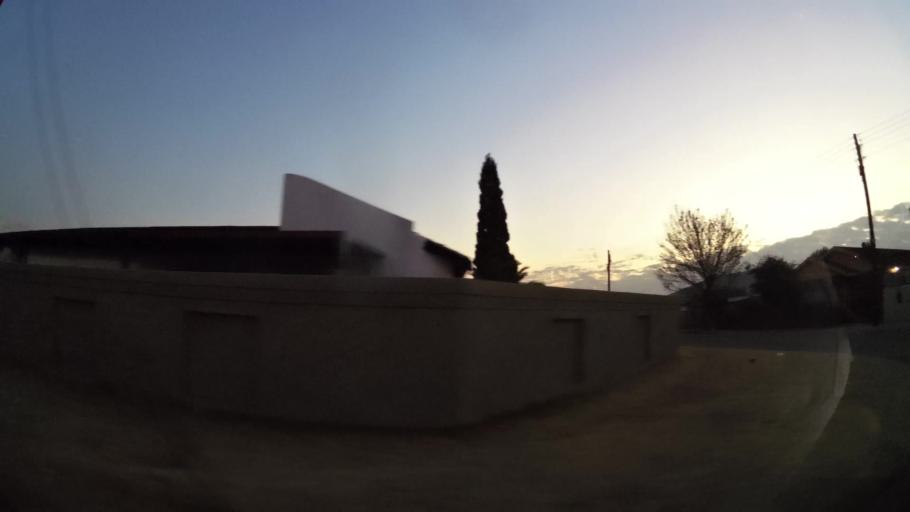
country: ZA
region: Gauteng
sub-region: West Rand District Municipality
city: Randfontein
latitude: -26.2060
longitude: 27.7053
